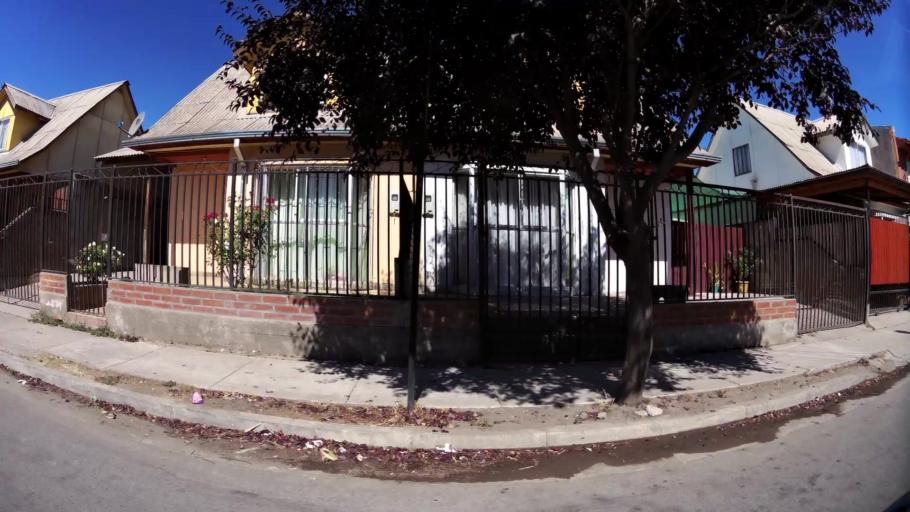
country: CL
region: O'Higgins
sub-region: Provincia de Colchagua
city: Chimbarongo
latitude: -34.5960
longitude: -71.0011
